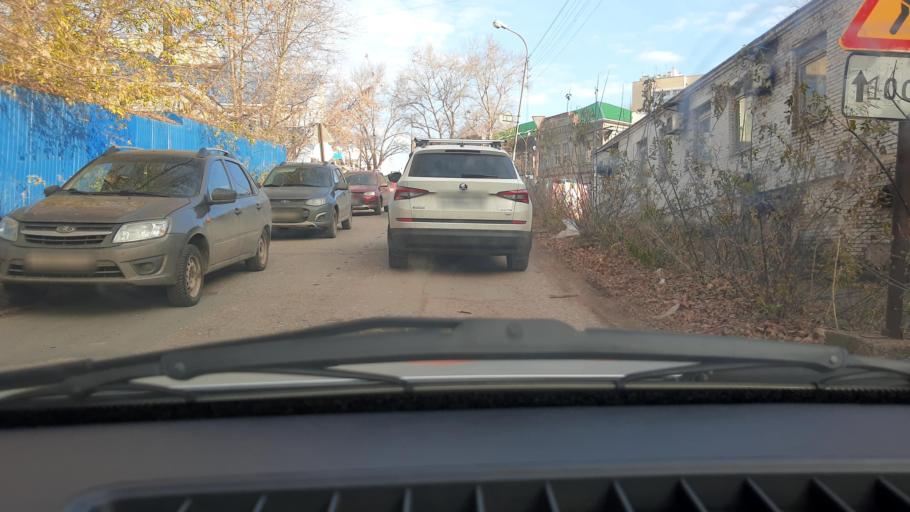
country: RU
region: Bashkortostan
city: Ufa
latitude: 54.7287
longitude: 55.9879
